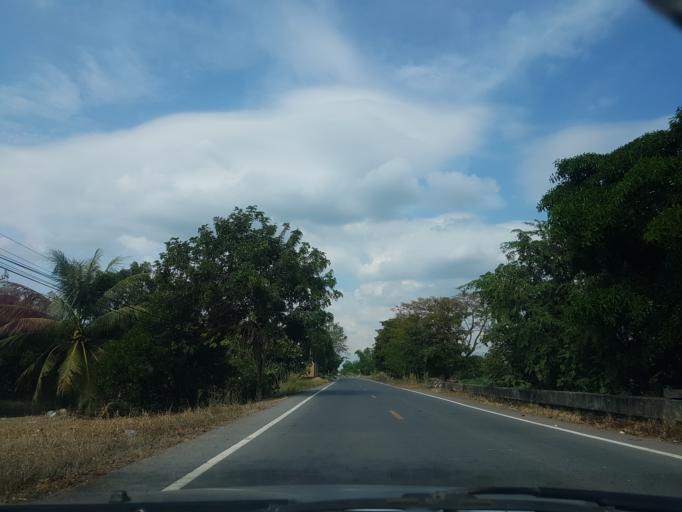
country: TH
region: Pathum Thani
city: Nong Suea
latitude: 14.1391
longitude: 100.8914
